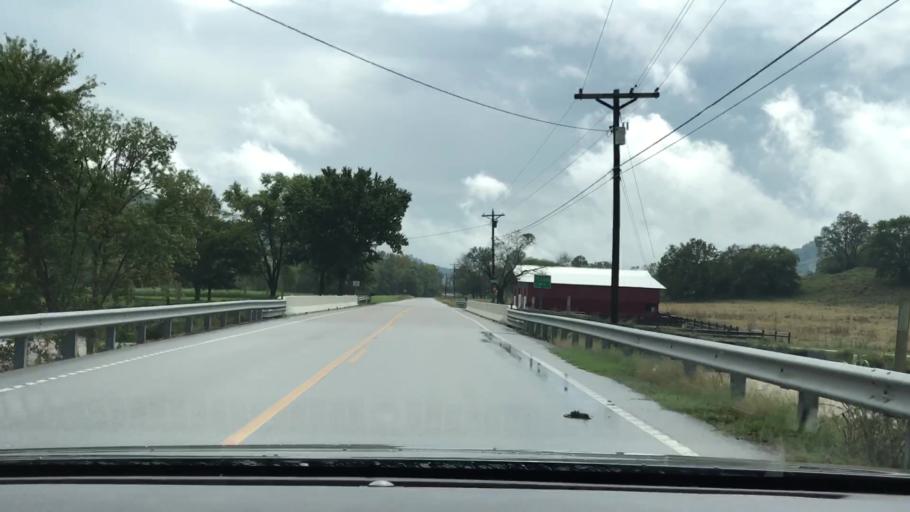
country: US
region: Tennessee
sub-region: Smith County
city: Carthage
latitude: 36.3482
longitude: -85.9653
